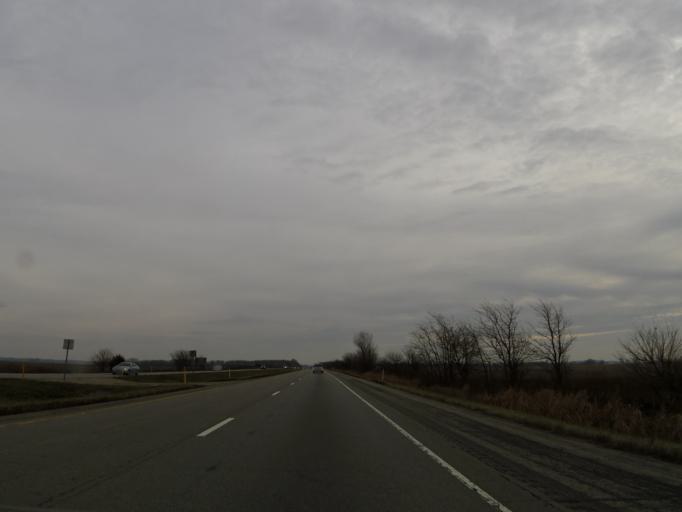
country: US
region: Illinois
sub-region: Vermilion County
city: Danville
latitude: 40.1175
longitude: -87.5210
